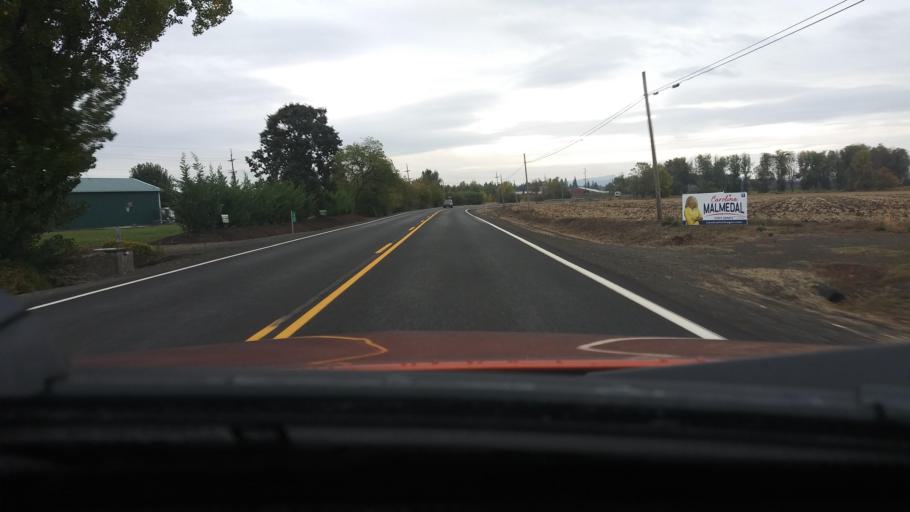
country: US
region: Oregon
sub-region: Washington County
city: Banks
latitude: 45.5770
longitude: -123.1106
